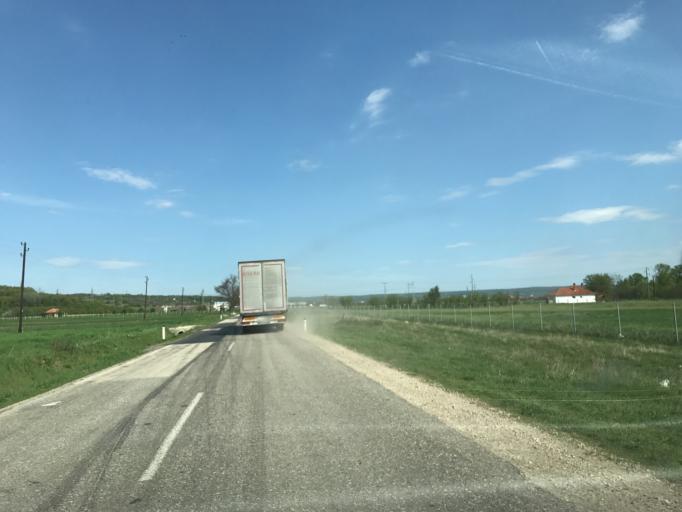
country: RS
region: Central Serbia
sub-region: Zajecarski Okrug
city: Zajecar
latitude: 43.9026
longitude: 22.2263
